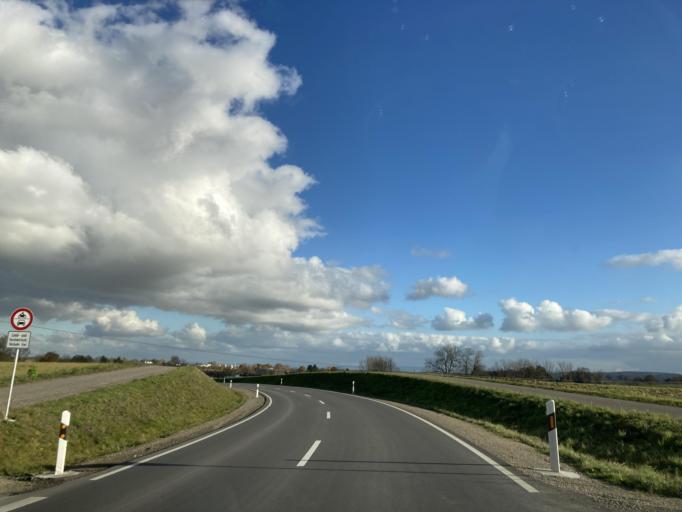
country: DE
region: Baden-Wuerttemberg
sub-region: Karlsruhe Region
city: Empfingen
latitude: 48.3997
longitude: 8.6898
